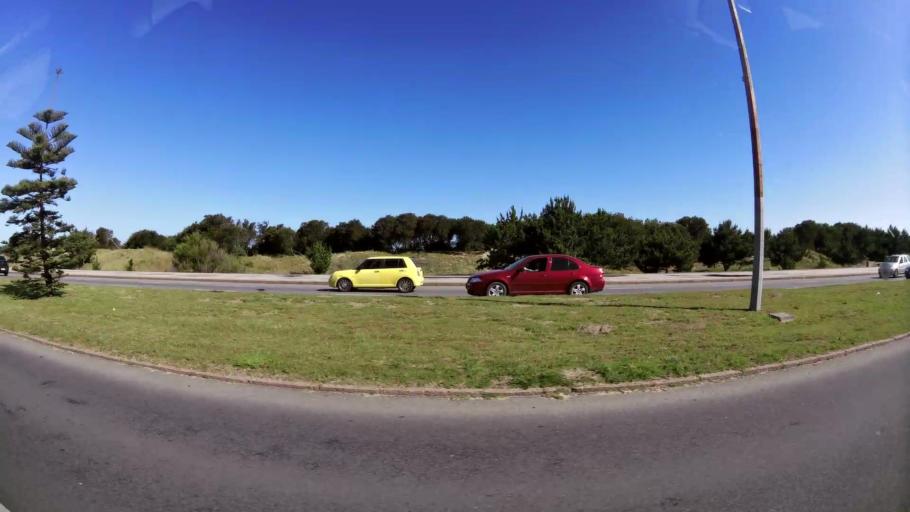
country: UY
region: Canelones
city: Barra de Carrasco
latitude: -34.8879
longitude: -56.0484
